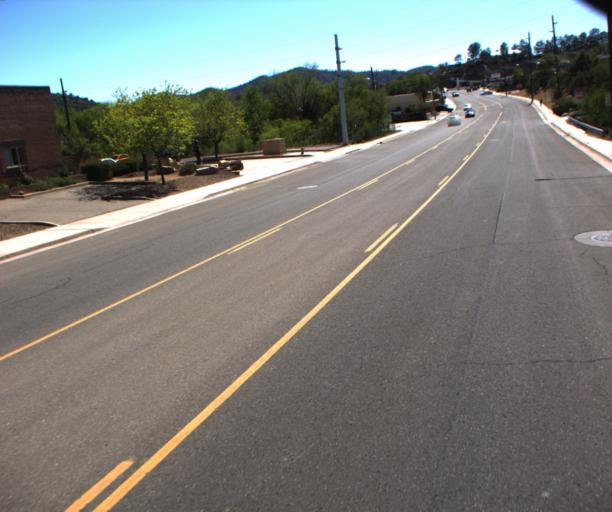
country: US
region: Arizona
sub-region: Yavapai County
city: Prescott
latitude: 34.5308
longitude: -112.4728
